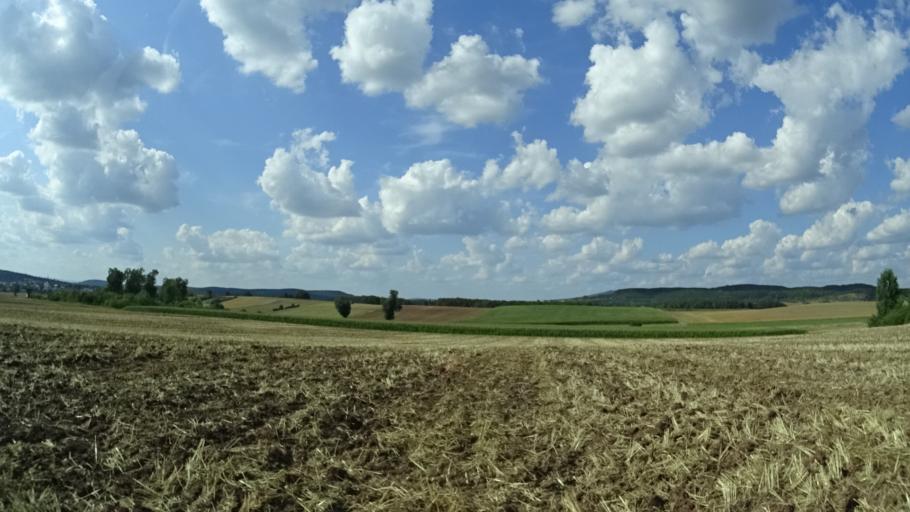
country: DE
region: Bavaria
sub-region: Regierungsbezirk Unterfranken
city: Trappstadt
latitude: 50.2860
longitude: 10.5846
